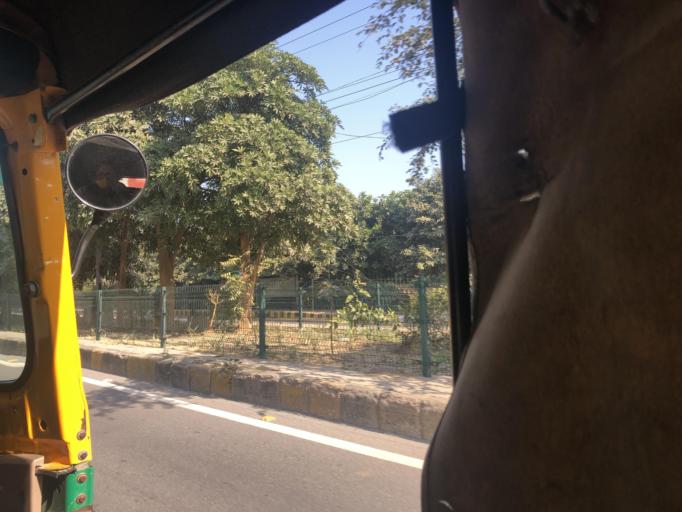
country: IN
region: Haryana
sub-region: Gurgaon
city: Gurgaon
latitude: 28.4354
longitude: 77.0903
